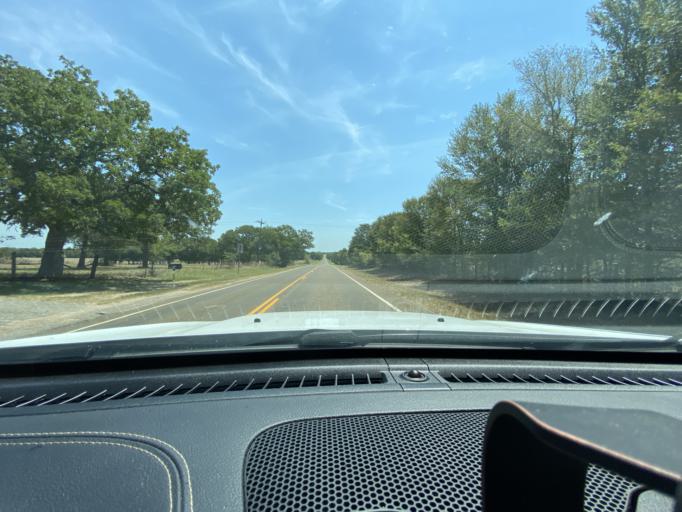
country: US
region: Texas
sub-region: Lee County
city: Giddings
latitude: 30.1377
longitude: -97.0749
